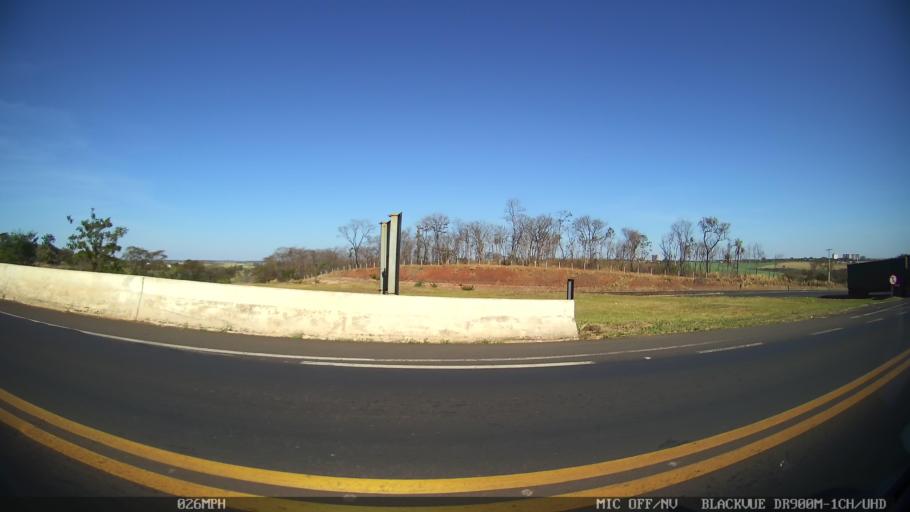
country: BR
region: Sao Paulo
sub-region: Olimpia
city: Olimpia
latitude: -20.6852
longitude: -48.9056
